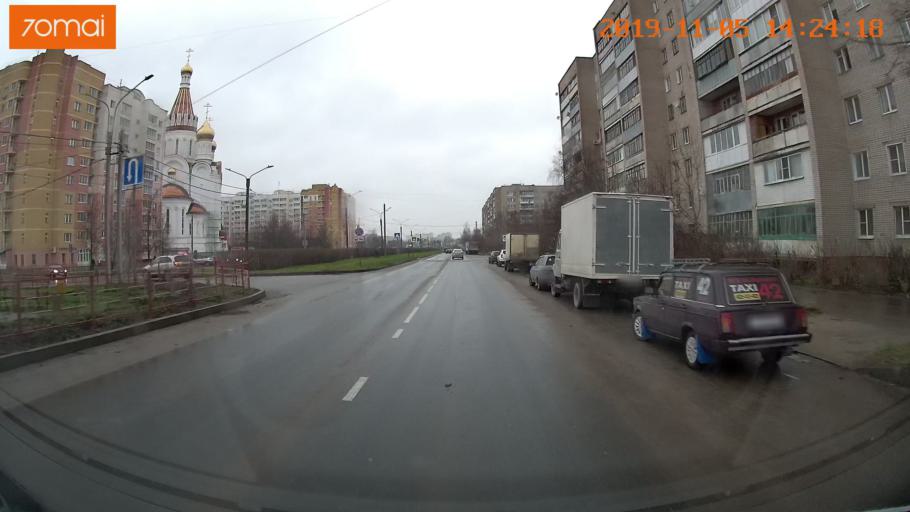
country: RU
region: Ivanovo
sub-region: Gorod Ivanovo
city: Ivanovo
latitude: 56.9681
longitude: 40.9981
